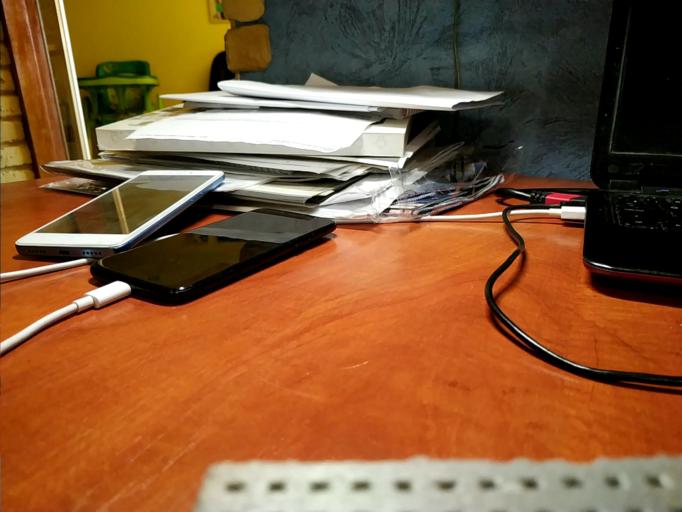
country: RU
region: Tverskaya
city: Kalashnikovo
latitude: 57.4052
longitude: 35.2016
